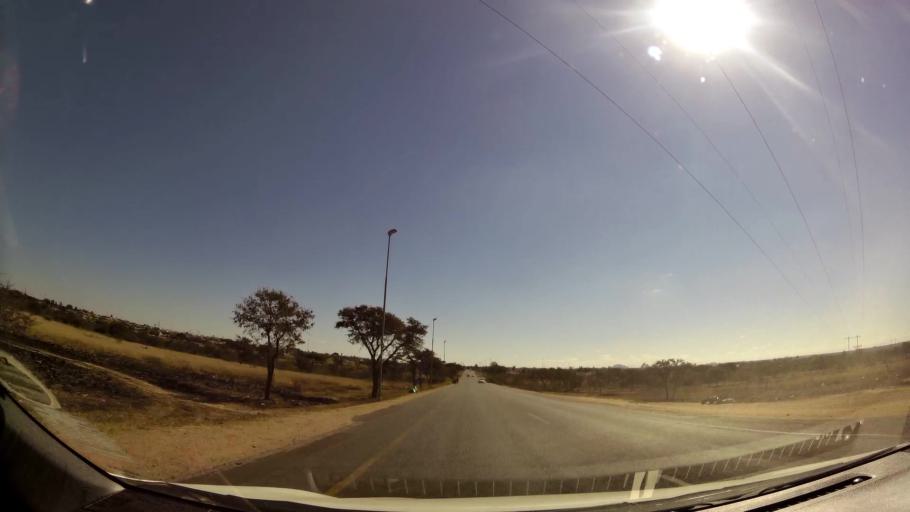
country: ZA
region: Limpopo
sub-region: Capricorn District Municipality
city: Polokwane
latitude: -23.8559
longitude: 29.4060
